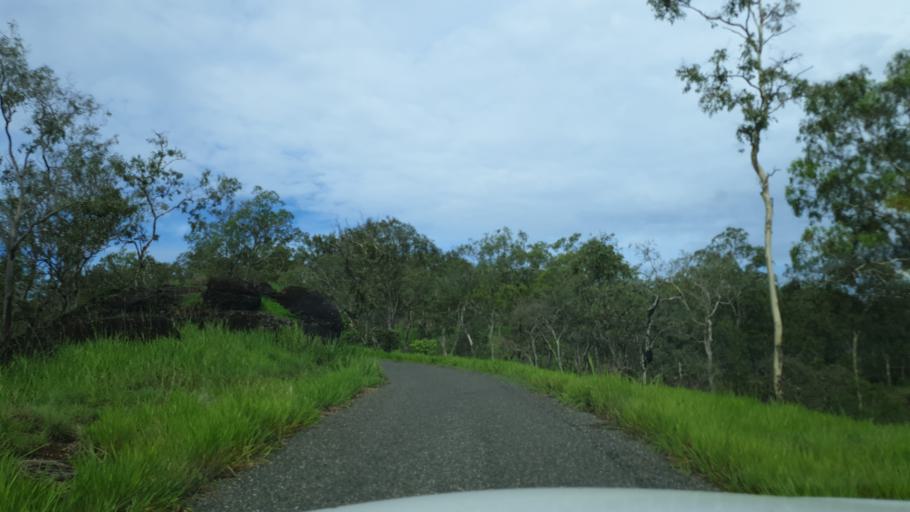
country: PG
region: National Capital
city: Port Moresby
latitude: -9.4345
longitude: 147.3804
